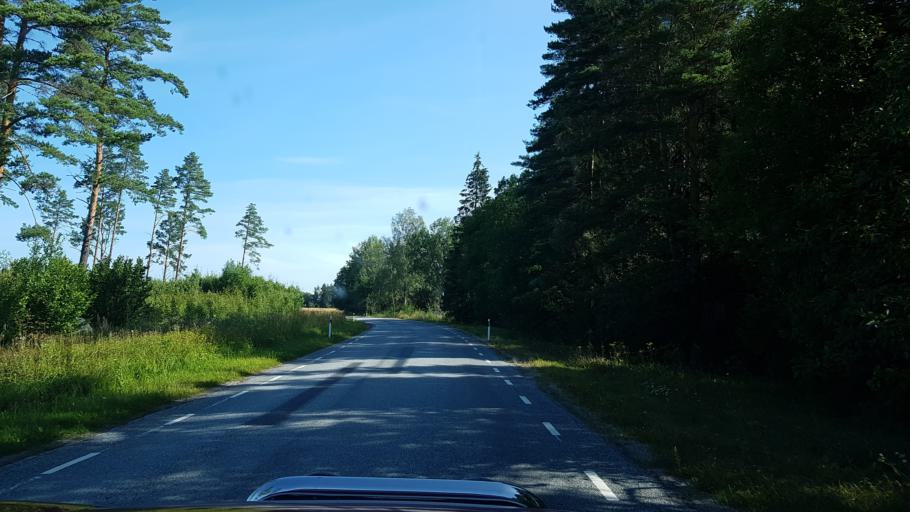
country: EE
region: Harju
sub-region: Raasiku vald
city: Raasiku
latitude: 59.2888
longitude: 25.1664
